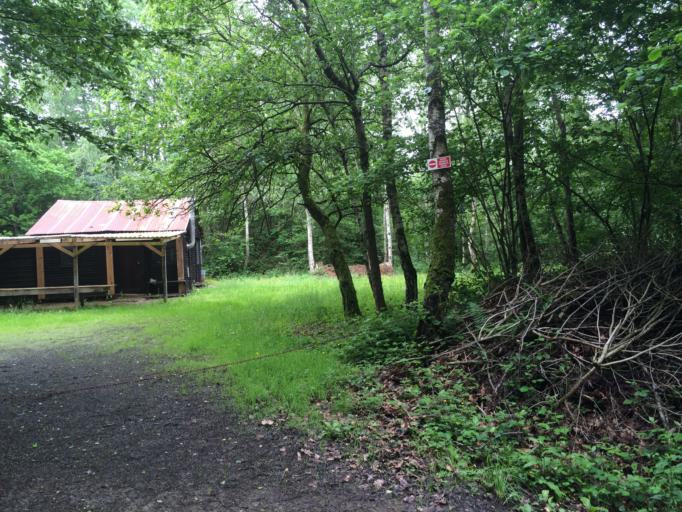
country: BE
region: Wallonia
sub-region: Province de Namur
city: Yvoir
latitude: 50.3263
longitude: 4.9510
